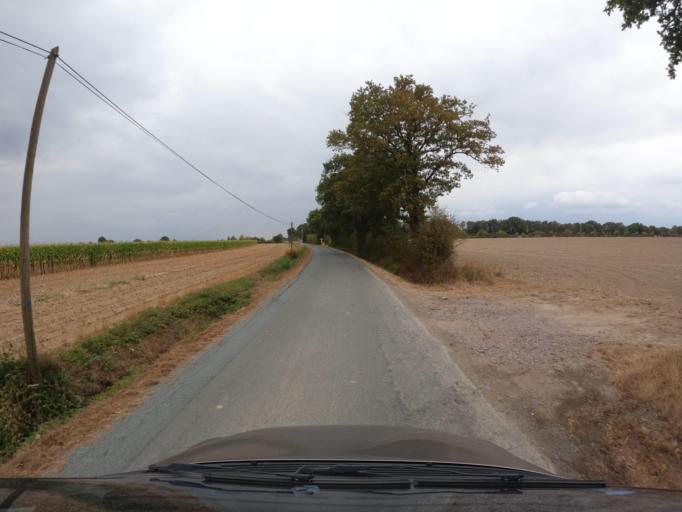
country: FR
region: Pays de la Loire
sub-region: Departement de la Vendee
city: Treize-Septiers
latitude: 46.9784
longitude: -1.2016
